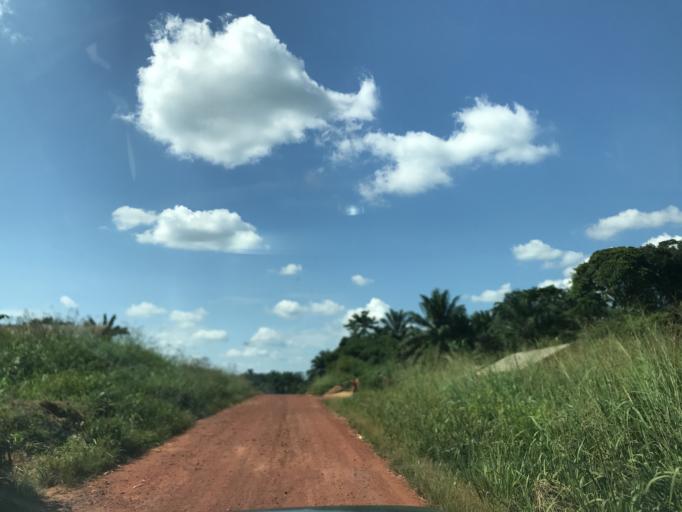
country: CD
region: Eastern Province
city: Kisangani
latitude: 1.2197
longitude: 25.2682
